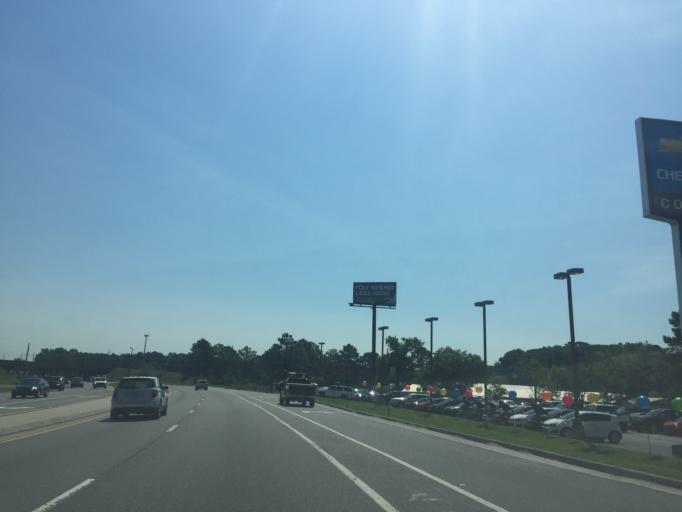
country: US
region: Georgia
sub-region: Chatham County
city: Georgetown
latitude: 31.9984
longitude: -81.2514
